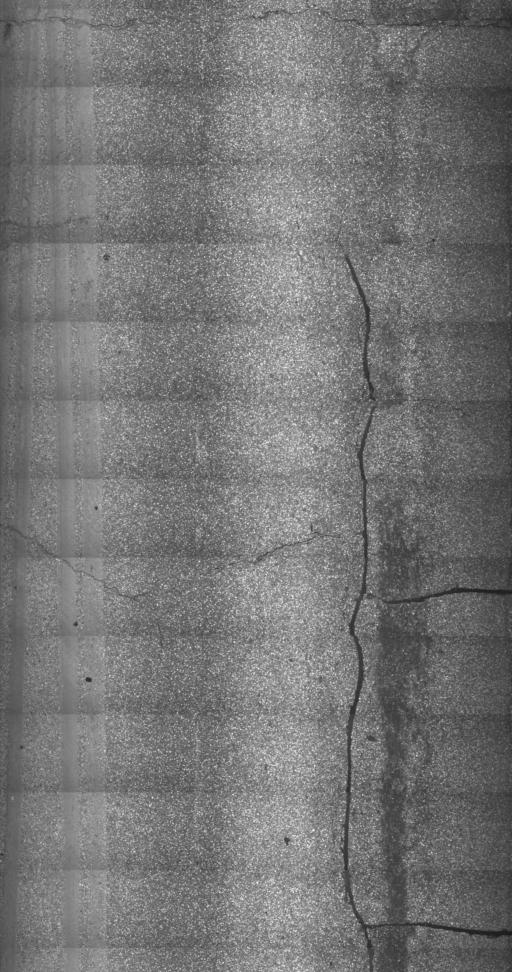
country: US
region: Vermont
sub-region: Bennington County
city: Manchester Center
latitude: 43.1726
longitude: -73.0465
